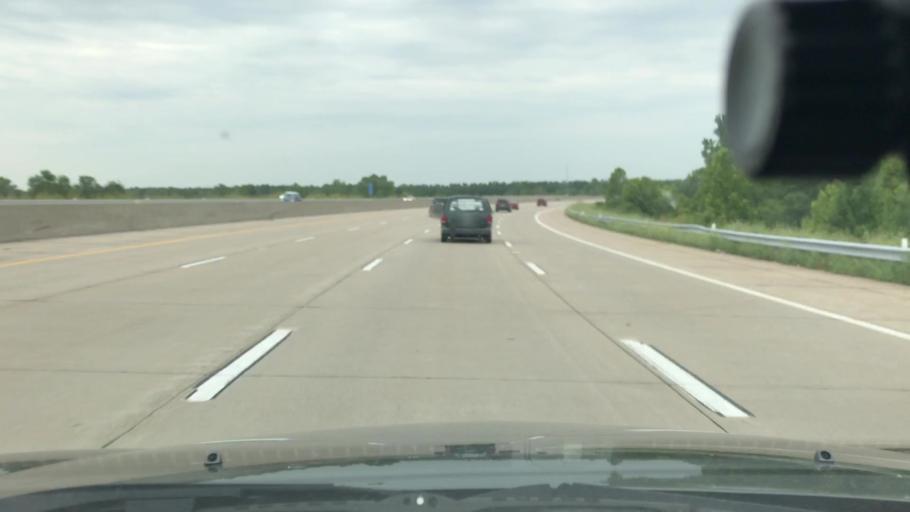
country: US
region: Missouri
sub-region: Saint Louis County
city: Maryland Heights
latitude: 38.7067
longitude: -90.4985
